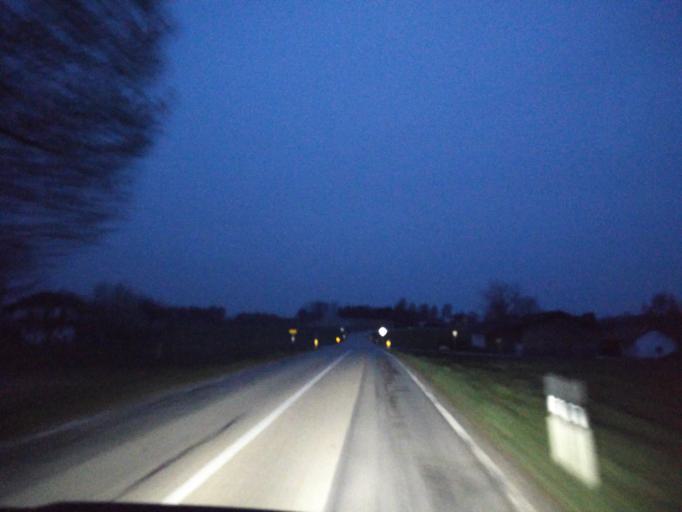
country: DE
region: Bavaria
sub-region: Upper Bavaria
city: Griesstatt
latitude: 47.9881
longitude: 12.1947
